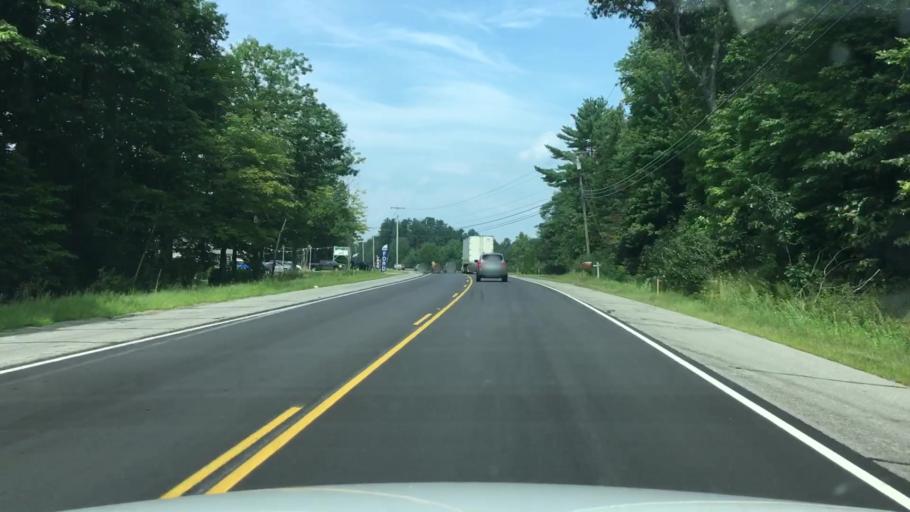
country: US
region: Maine
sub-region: Androscoggin County
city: Turner
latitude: 44.2230
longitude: -70.2489
